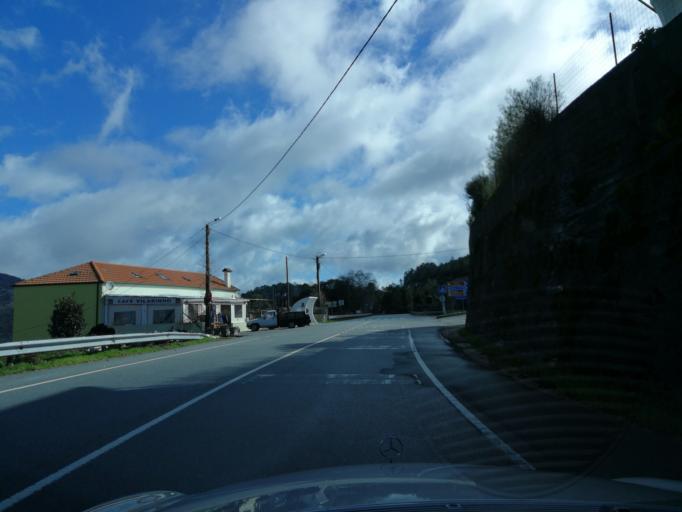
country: ES
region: Galicia
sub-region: Provincia de Ourense
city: Entrimo
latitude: 41.8686
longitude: -8.1992
